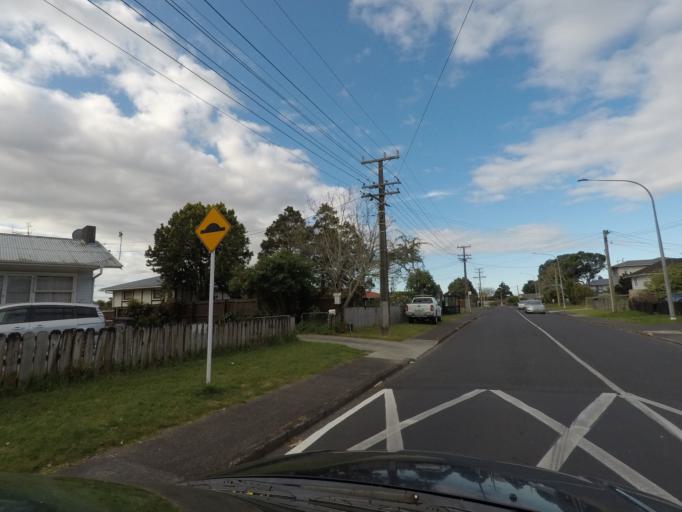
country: NZ
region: Auckland
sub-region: Auckland
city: Rosebank
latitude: -36.8864
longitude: 174.6550
